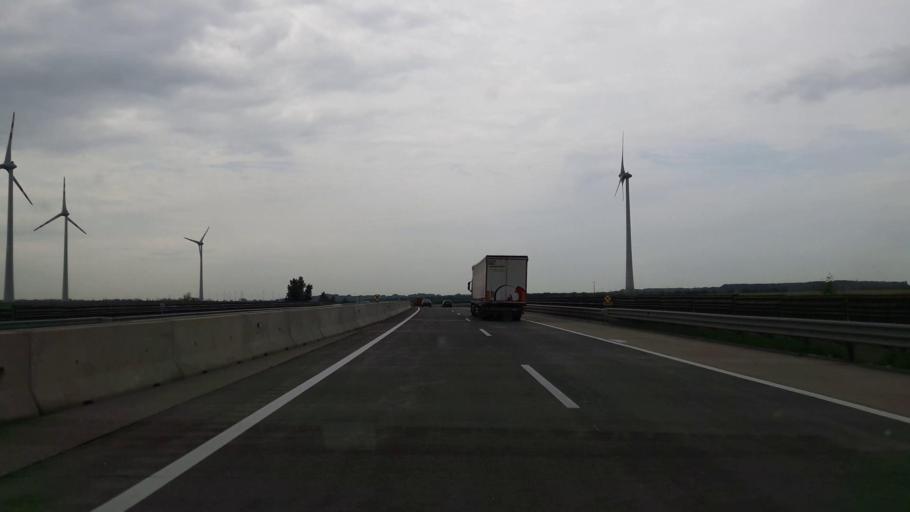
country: AT
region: Burgenland
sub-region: Politischer Bezirk Neusiedl am See
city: Pama
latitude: 48.0519
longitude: 16.9960
